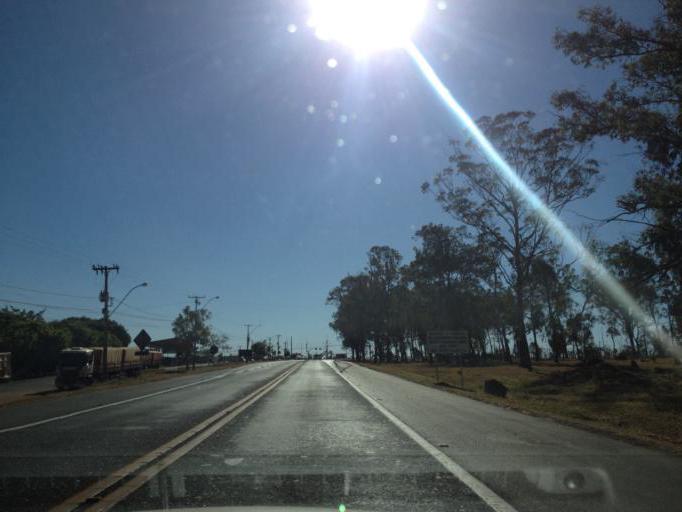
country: BR
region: Federal District
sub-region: Brasilia
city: Brasilia
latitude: -15.6904
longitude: -47.8557
